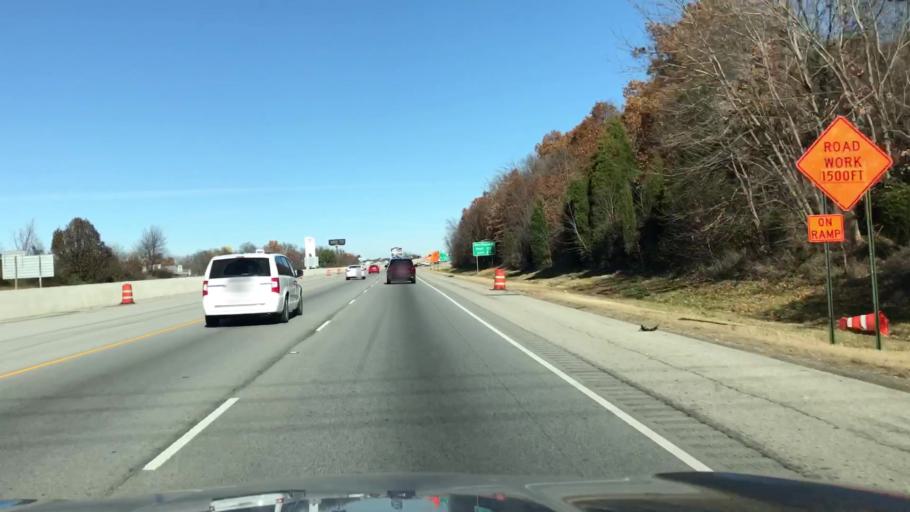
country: US
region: Arkansas
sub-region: Benton County
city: Bentonville
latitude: 36.3282
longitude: -94.1845
